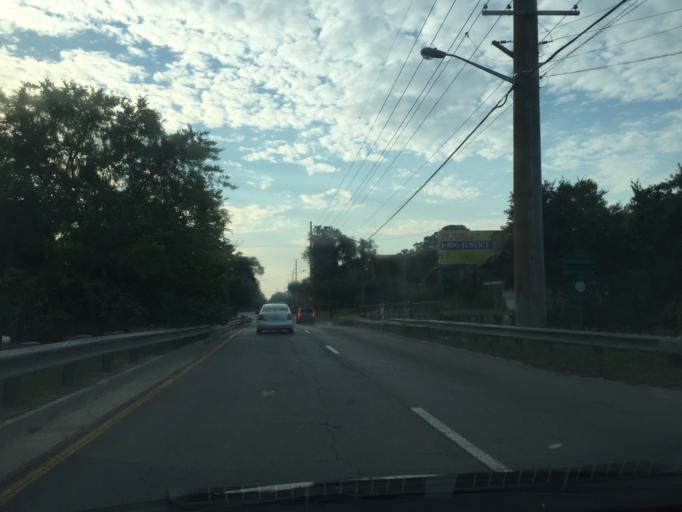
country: US
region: Georgia
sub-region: Chatham County
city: Isle of Hope
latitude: 31.9932
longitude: -81.1018
